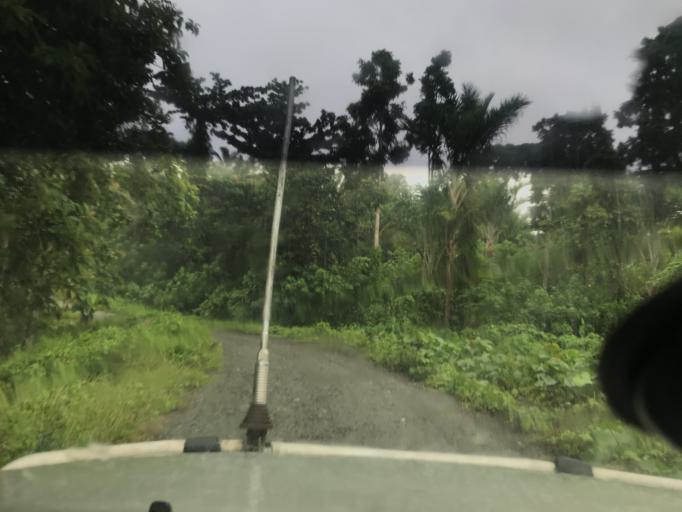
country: SB
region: Malaita
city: Auki
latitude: -9.0731
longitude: 160.8132
